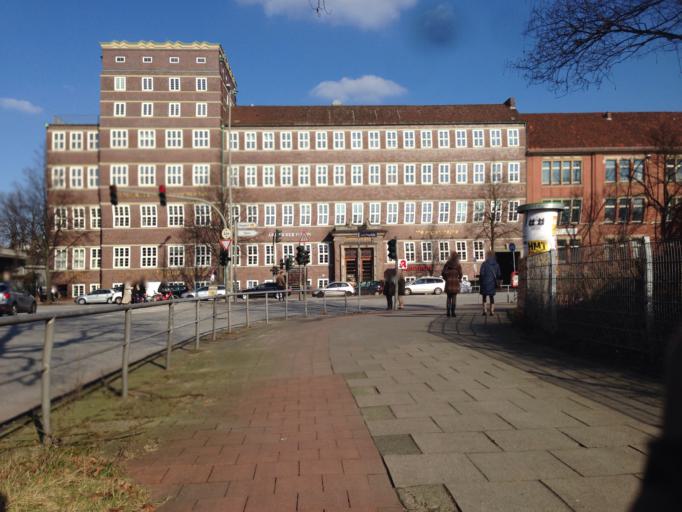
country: DE
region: Hamburg
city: Hamburg
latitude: 53.5690
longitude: 10.0277
